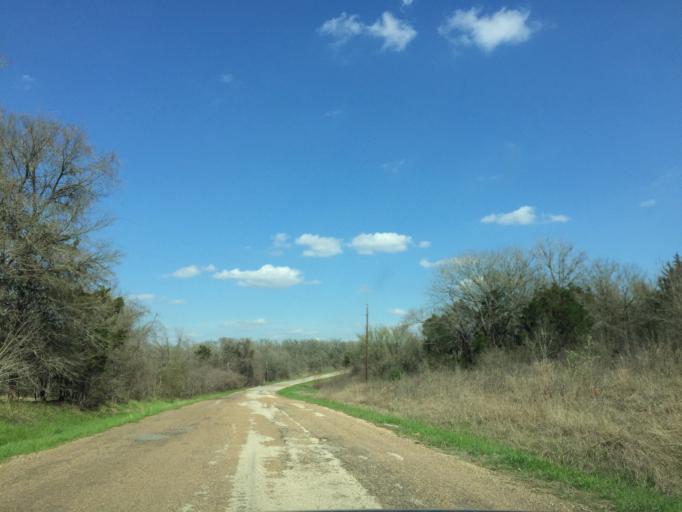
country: US
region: Texas
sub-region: Milam County
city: Thorndale
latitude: 30.5580
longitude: -97.1755
